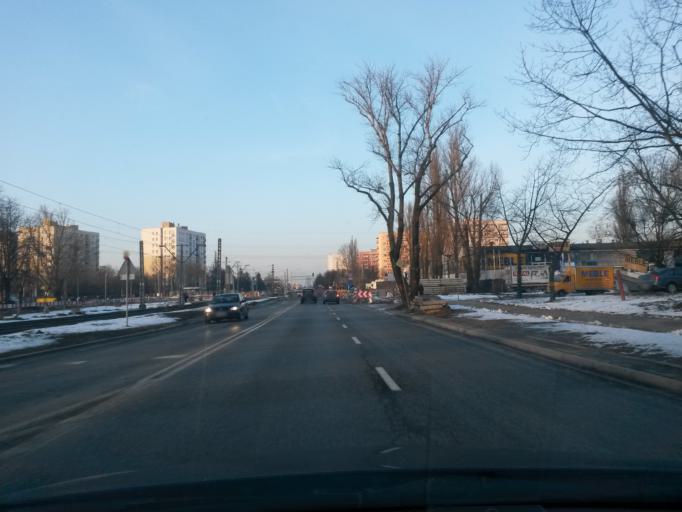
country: PL
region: Masovian Voivodeship
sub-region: Warszawa
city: Mokotow
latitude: 52.1872
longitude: 21.0023
